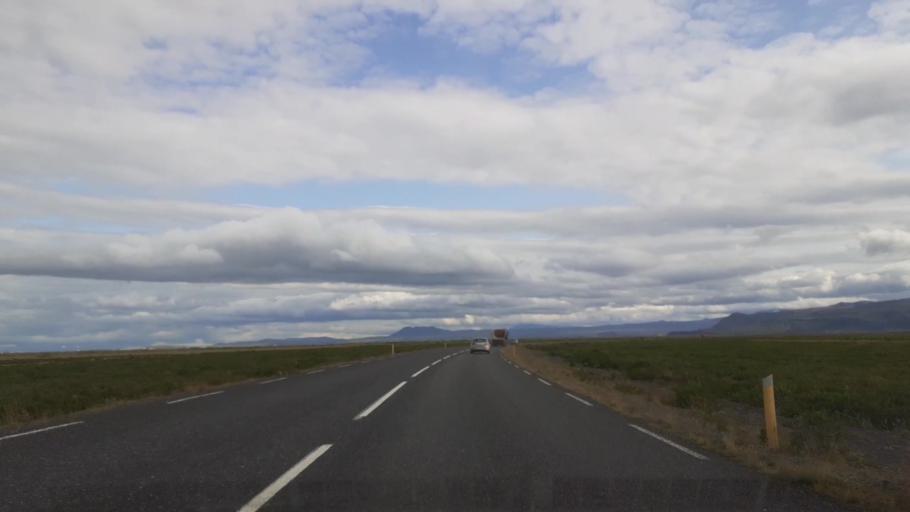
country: IS
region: South
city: Vestmannaeyjar
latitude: 63.5355
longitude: -20.1184
